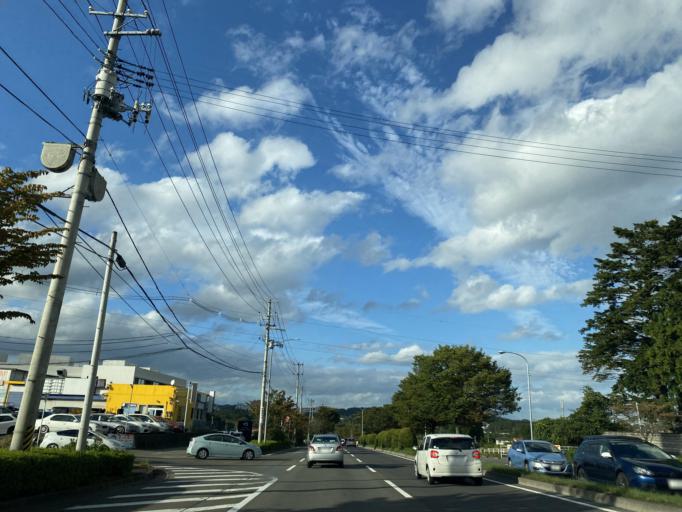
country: JP
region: Miyagi
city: Sendai-shi
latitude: 38.3200
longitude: 140.8445
